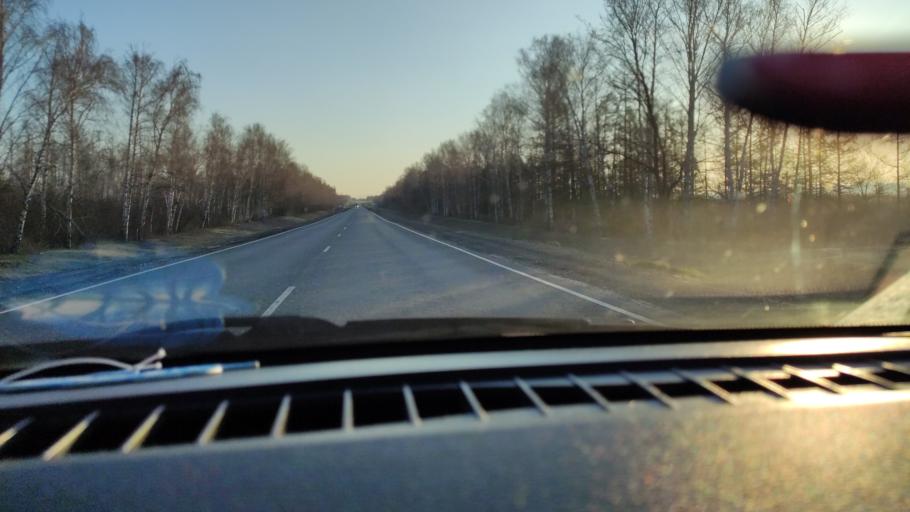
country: RU
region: Saratov
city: Sennoy
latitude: 52.1254
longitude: 46.8529
